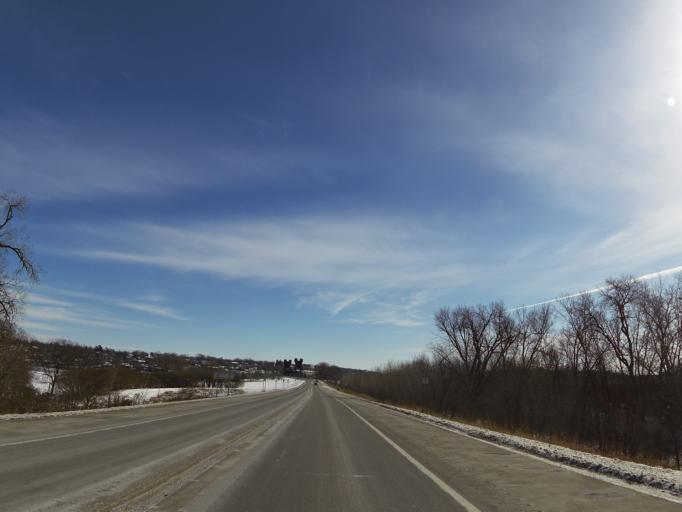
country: US
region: Wisconsin
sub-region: Pierce County
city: Prescott
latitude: 44.7499
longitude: -92.8152
